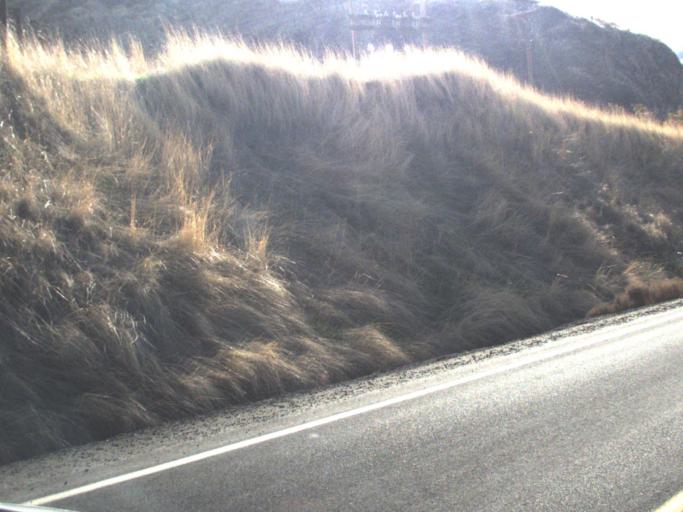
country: US
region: Washington
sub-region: Whitman County
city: Colfax
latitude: 46.7043
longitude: -117.4670
